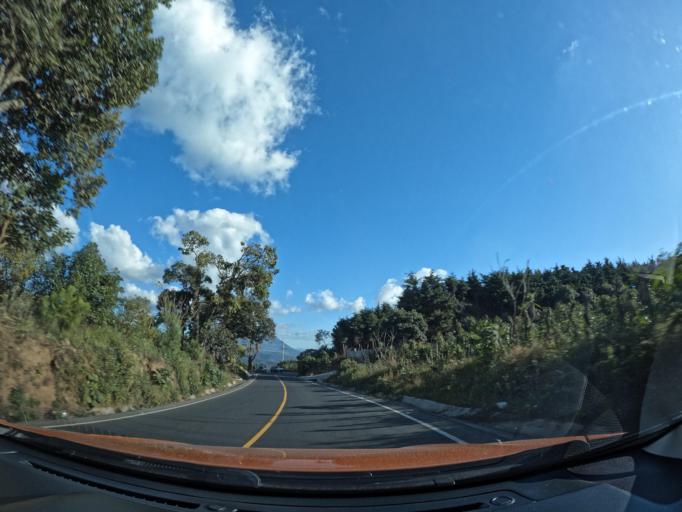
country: GT
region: Sacatepequez
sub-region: Municipio de Santa Maria de Jesus
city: Santa Maria de Jesus
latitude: 14.4712
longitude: -90.6925
